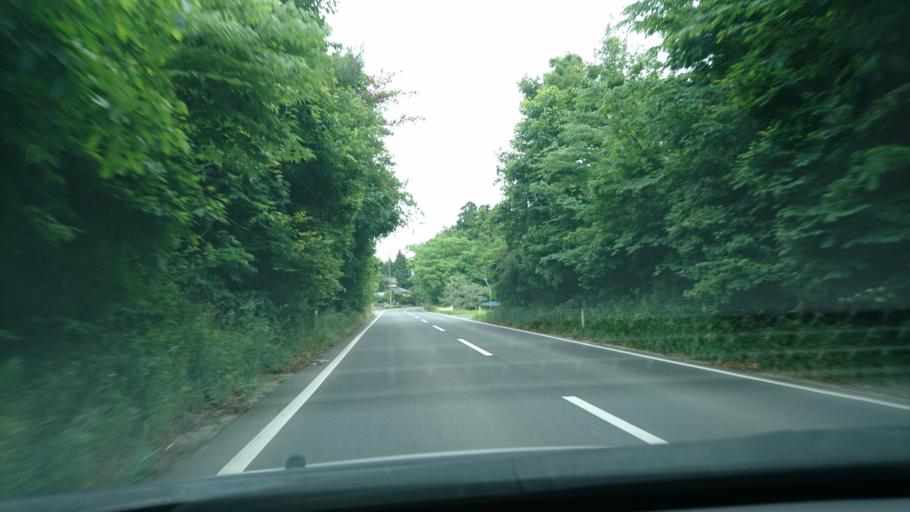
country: JP
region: Iwate
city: Ichinoseki
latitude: 38.7581
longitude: 141.2566
